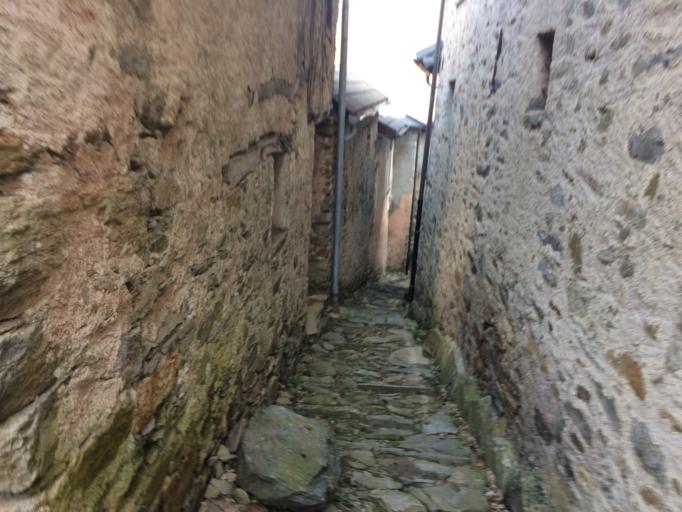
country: IT
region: Piedmont
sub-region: Provincia Verbano-Cusio-Ossola
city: Falmenta
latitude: 46.0675
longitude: 8.5951
